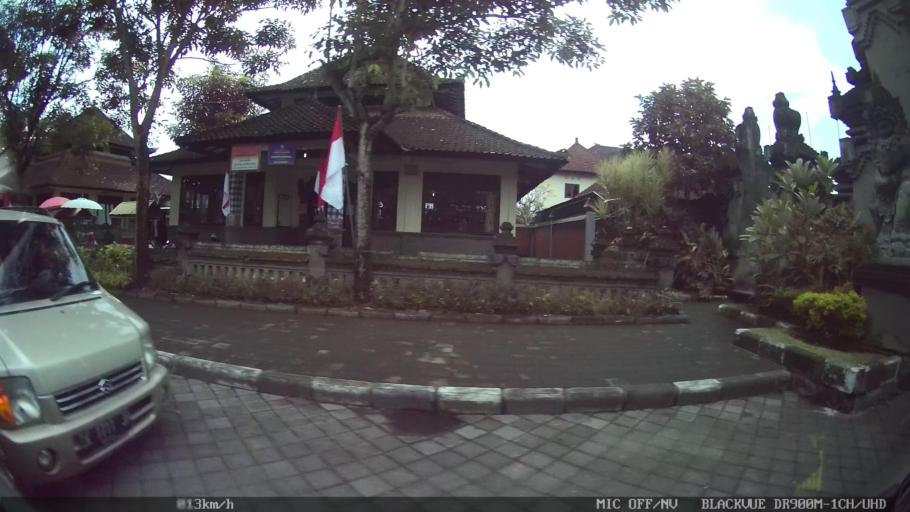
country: ID
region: Bali
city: Banjar Serangan
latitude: -8.5440
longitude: 115.1705
